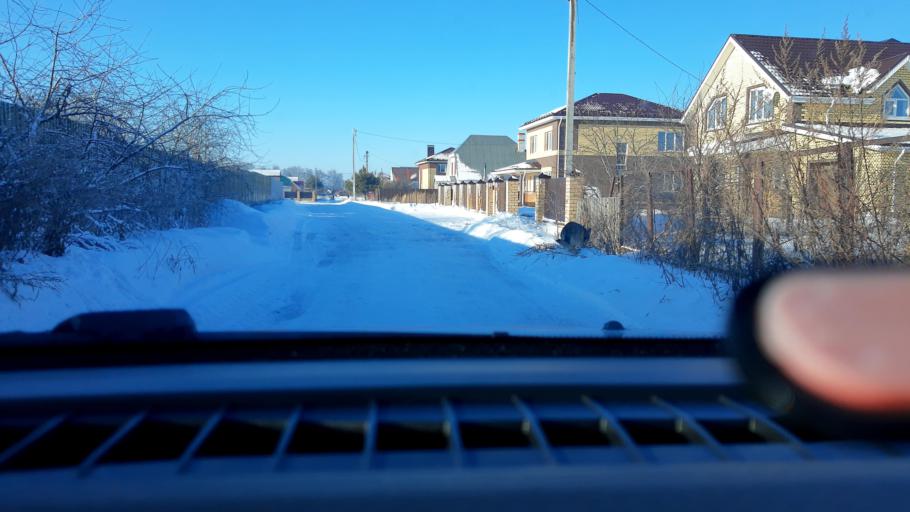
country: RU
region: Nizjnij Novgorod
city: Burevestnik
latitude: 56.1429
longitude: 43.9204
